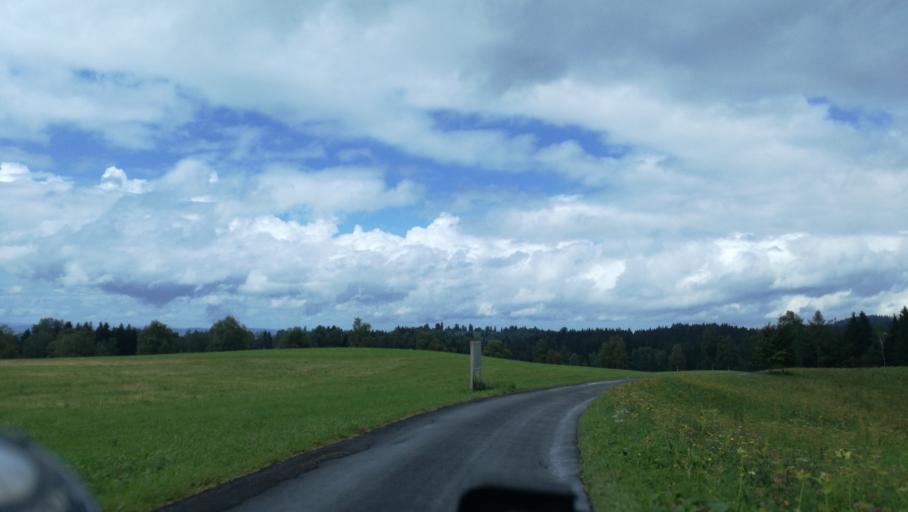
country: CH
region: Zug
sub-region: Zug
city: Walchwil
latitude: 47.1142
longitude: 8.5415
